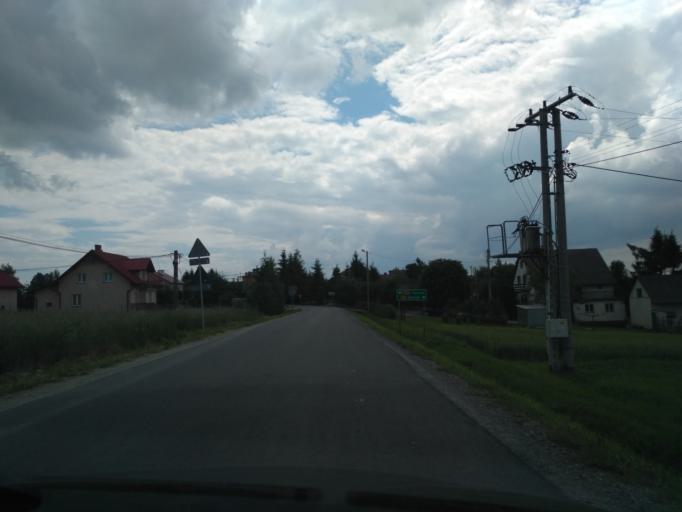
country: PL
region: Subcarpathian Voivodeship
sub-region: Powiat rzeszowski
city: Hyzne
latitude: 49.9328
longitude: 22.1842
